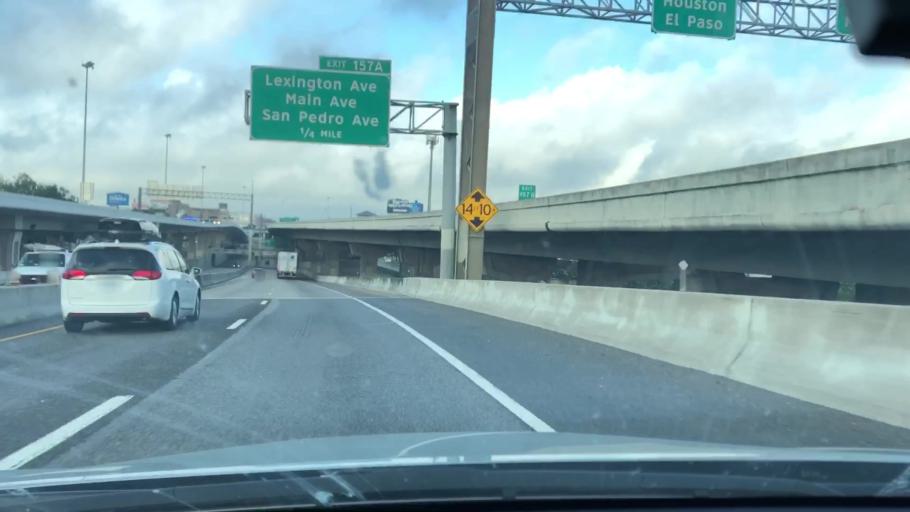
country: US
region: Texas
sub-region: Bexar County
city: San Antonio
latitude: 29.4402
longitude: -98.4868
